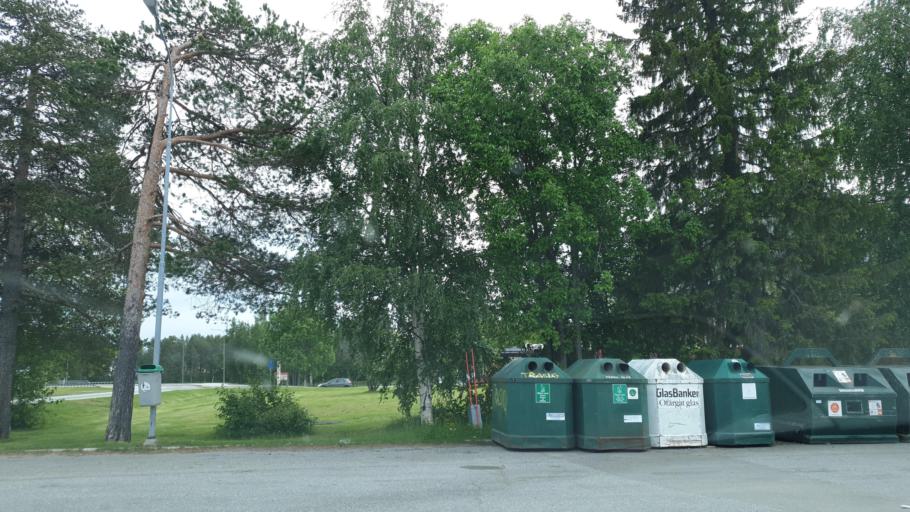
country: SE
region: Vaesterbotten
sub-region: Sorsele Kommun
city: Sorsele
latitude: 65.5363
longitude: 17.5312
